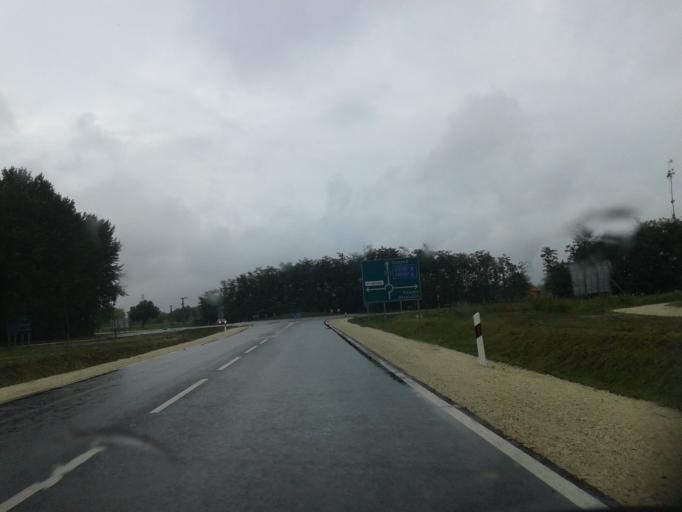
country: HU
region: Csongrad
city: Morahalom
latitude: 46.2246
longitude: 19.9076
